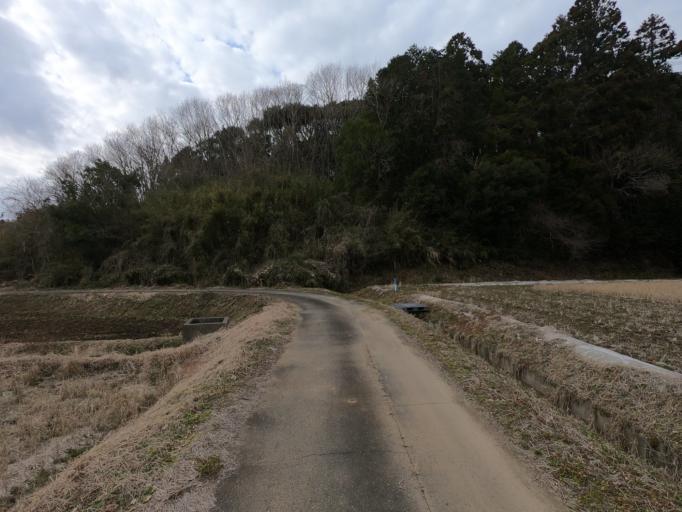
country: JP
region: Ibaraki
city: Inashiki
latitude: 36.0604
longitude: 140.4461
